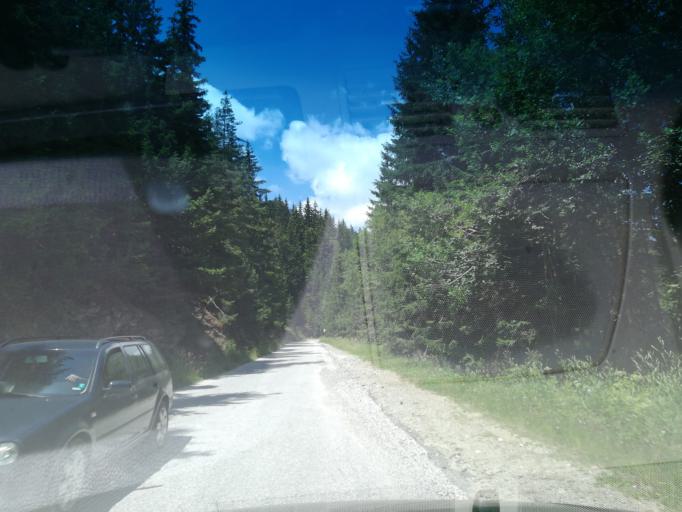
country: BG
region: Smolyan
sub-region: Obshtina Chepelare
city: Chepelare
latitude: 41.6874
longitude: 24.7726
